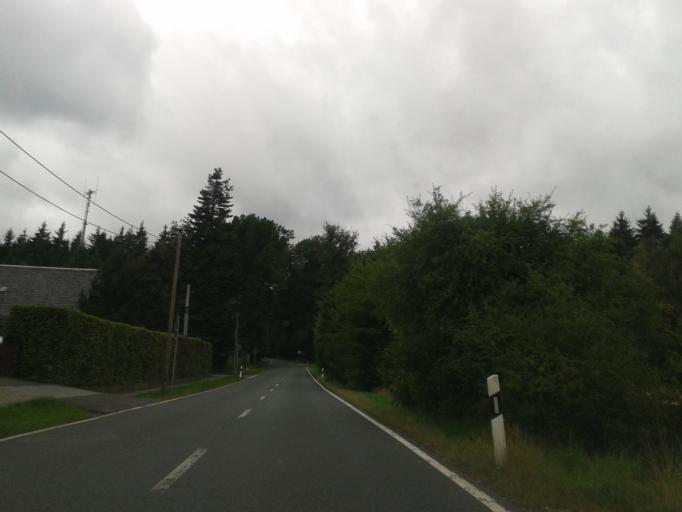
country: DE
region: Saxony
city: Dorfhain
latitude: 50.9519
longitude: 13.5027
